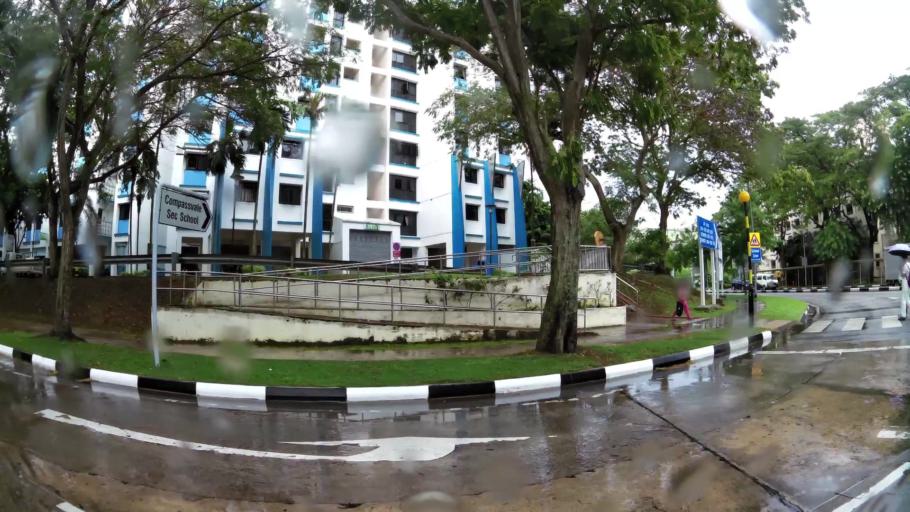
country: MY
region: Johor
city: Kampung Pasir Gudang Baru
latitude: 1.3951
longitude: 103.8989
